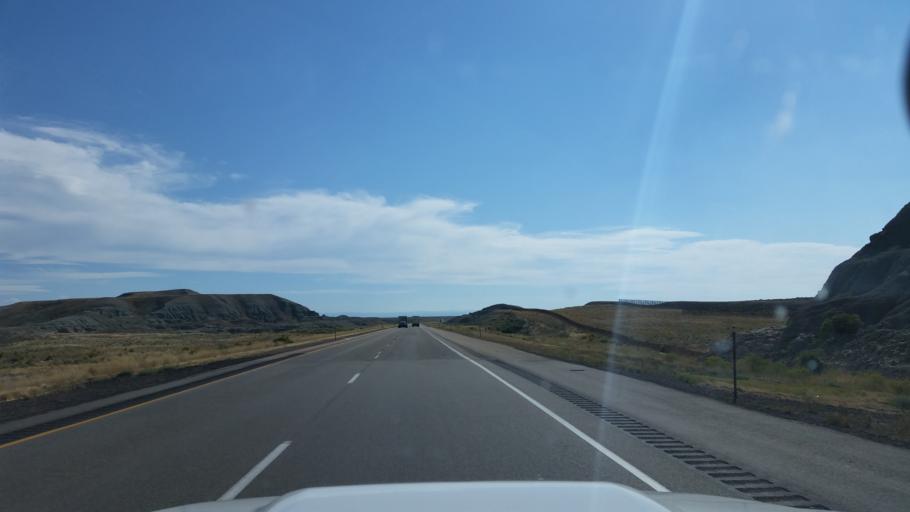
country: US
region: Wyoming
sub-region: Uinta County
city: Lyman
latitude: 41.4193
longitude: -110.1384
